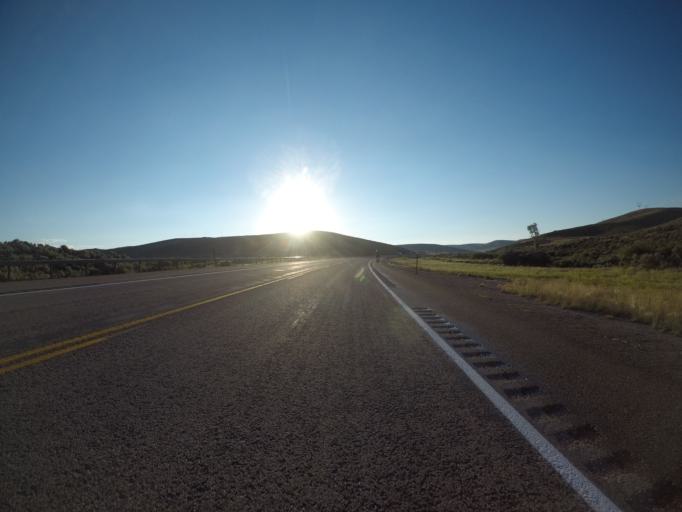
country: US
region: Wyoming
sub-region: Lincoln County
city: Kemmerer
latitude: 41.8722
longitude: -110.5217
